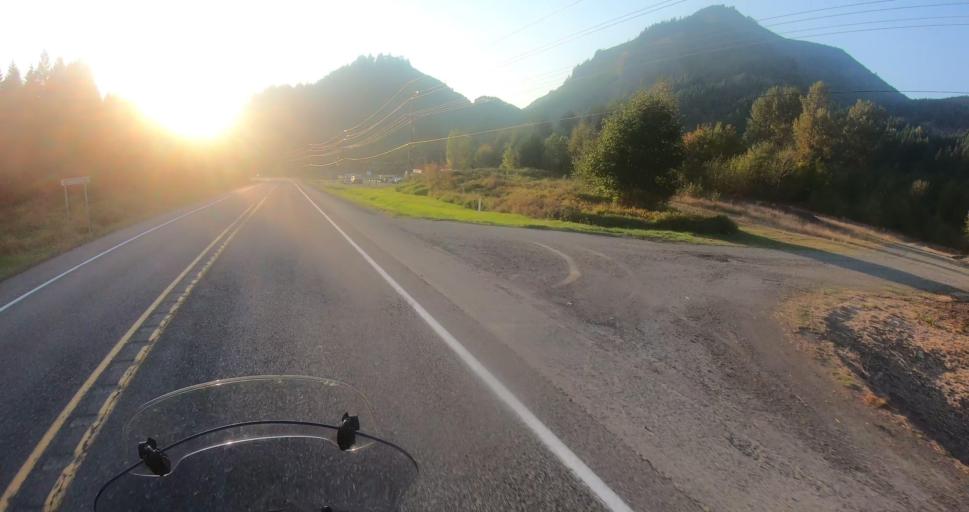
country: US
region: Washington
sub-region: Lewis County
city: Morton
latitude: 46.5391
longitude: -121.9905
